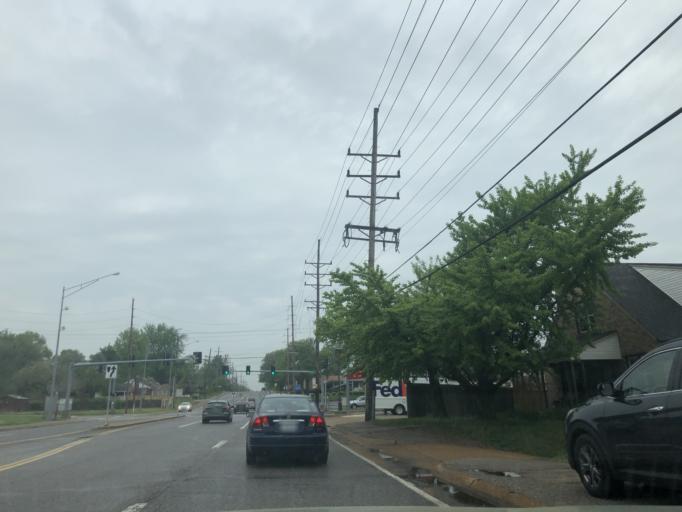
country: US
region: Missouri
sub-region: Saint Louis County
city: Marlborough
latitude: 38.5649
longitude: -90.3209
